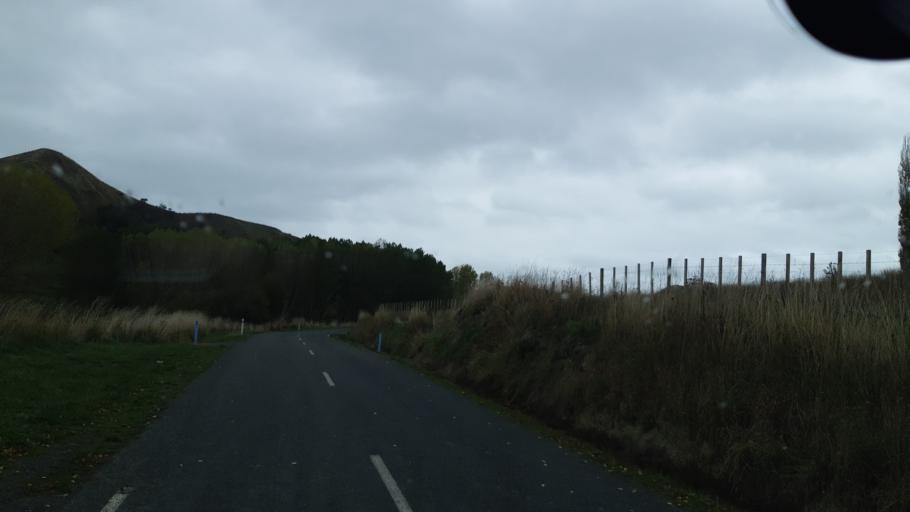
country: NZ
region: Manawatu-Wanganui
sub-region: Ruapehu District
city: Waiouru
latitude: -39.6121
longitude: 175.6077
